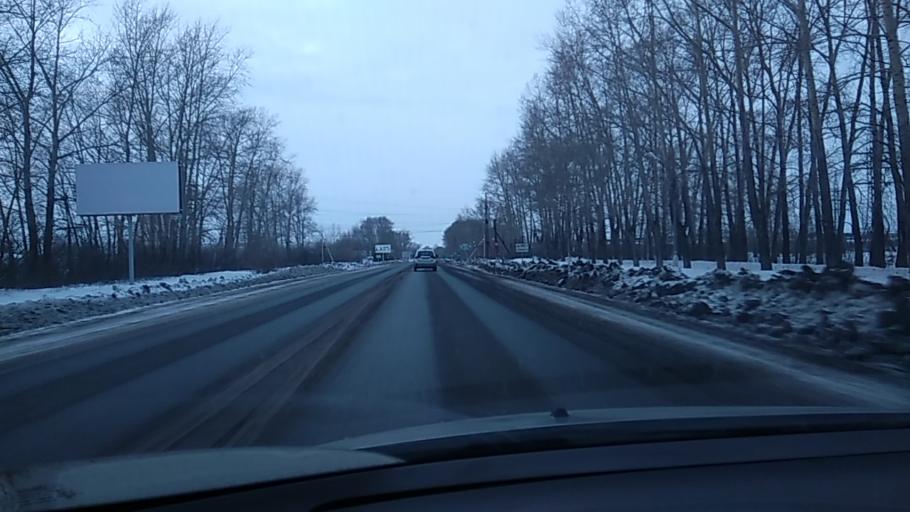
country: RU
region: Sverdlovsk
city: Martyush
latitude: 56.4422
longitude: 61.8289
